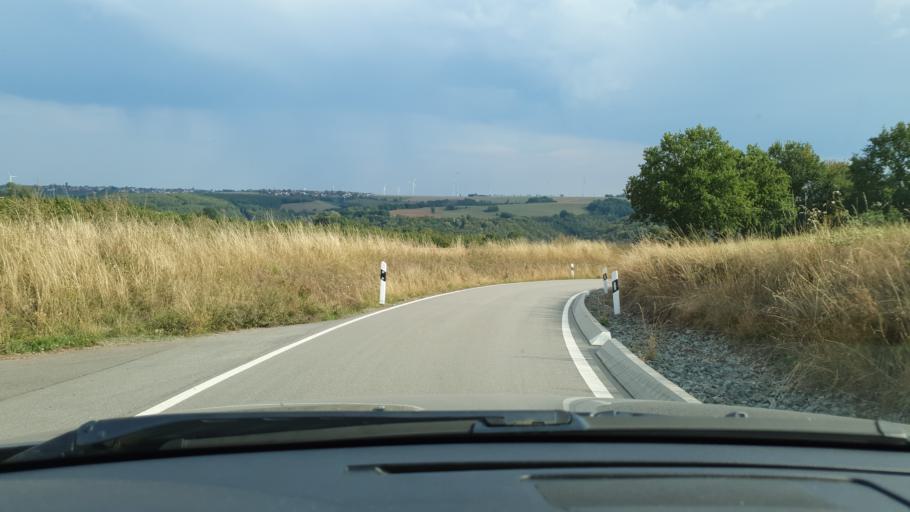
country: DE
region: Rheinland-Pfalz
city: Hettenhausen
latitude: 49.3448
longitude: 7.5526
